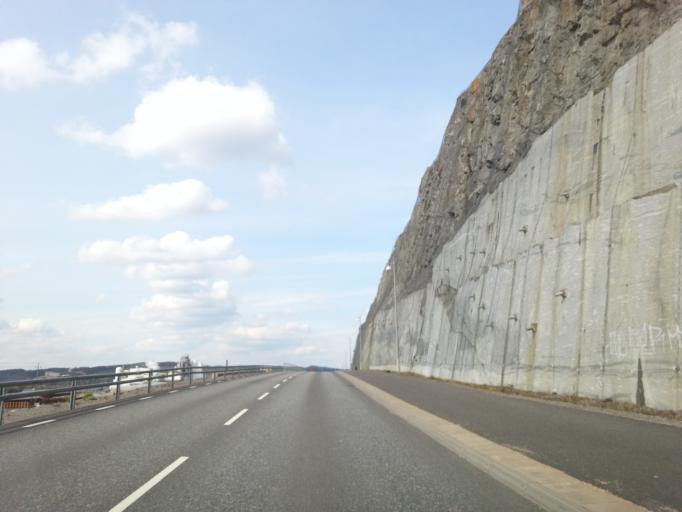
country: SE
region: Vaestra Goetaland
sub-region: Ale Kommun
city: Surte
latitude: 57.8417
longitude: 12.0140
